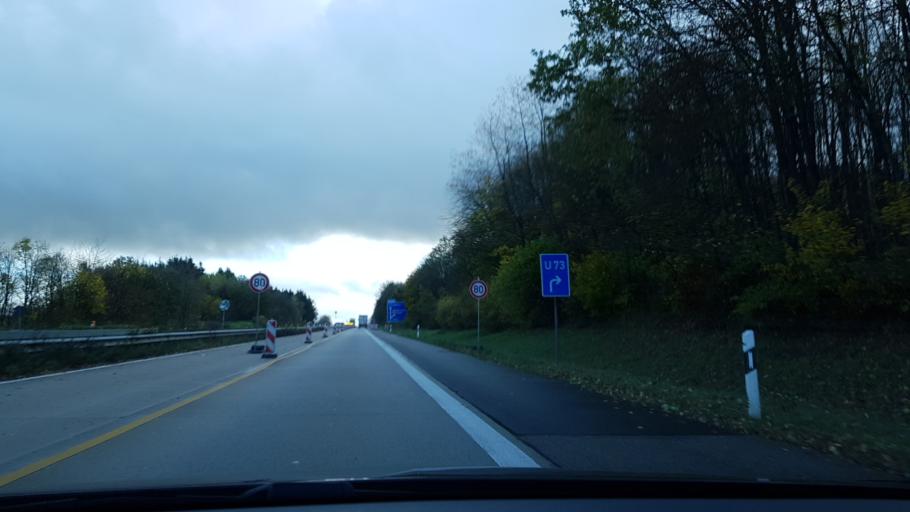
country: DE
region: Rheinland-Pfalz
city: Eckfeld
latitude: 50.1075
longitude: 6.8575
